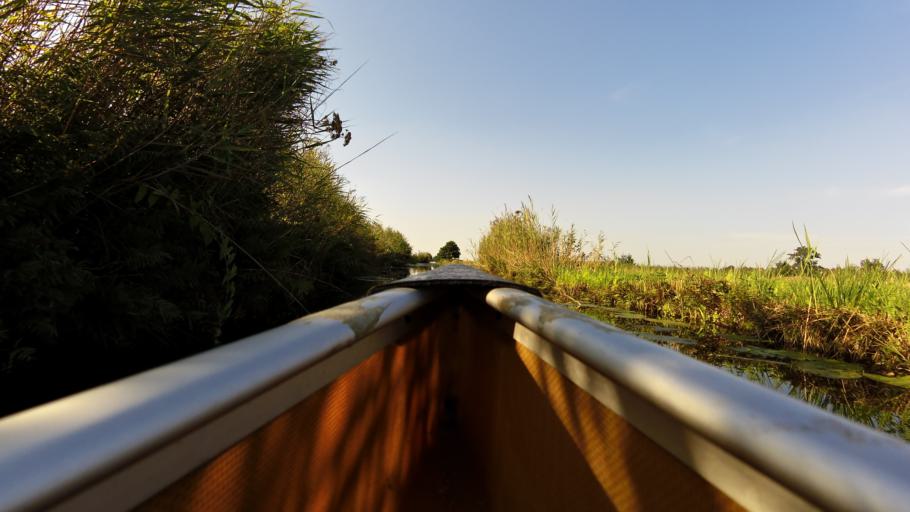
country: NL
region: South Holland
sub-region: Gemeente Nieuwkoop
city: Nieuwkoop
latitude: 52.1456
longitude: 4.8006
